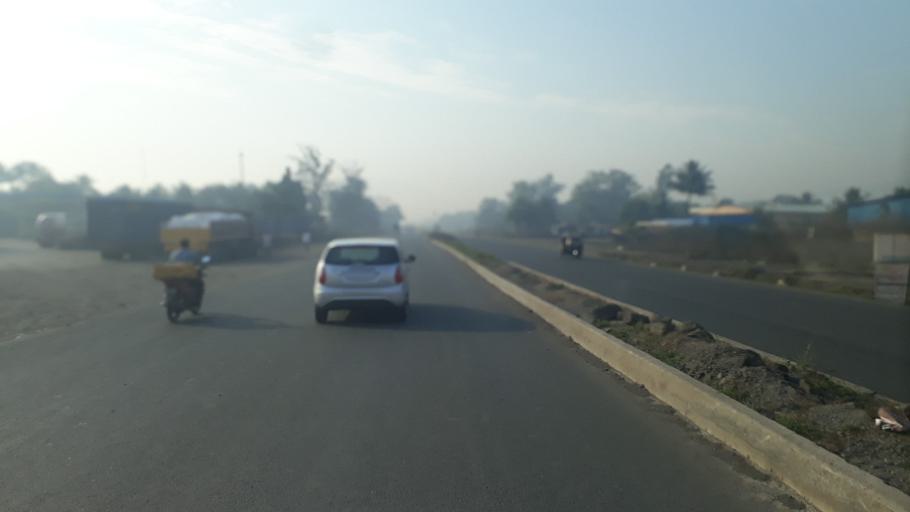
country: IN
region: Maharashtra
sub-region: Raigarh
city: Kalundri
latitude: 18.9507
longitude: 73.1307
